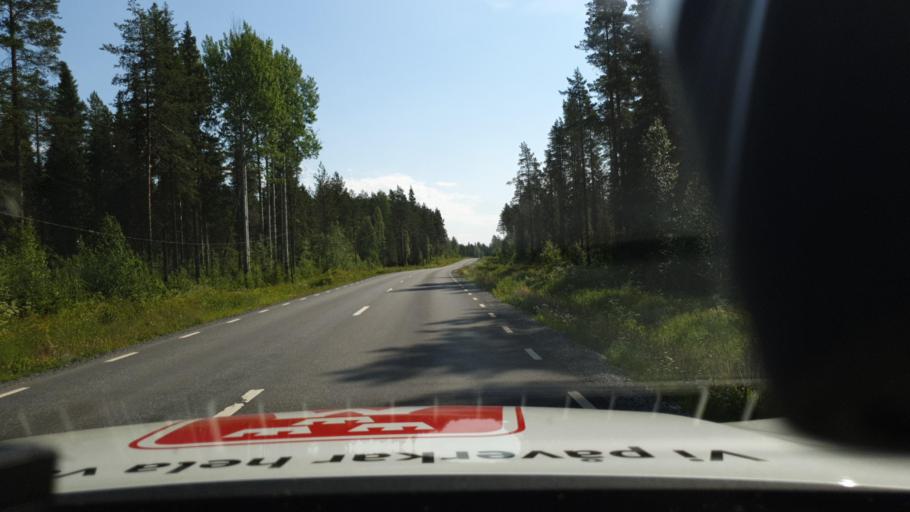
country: SE
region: Norrbotten
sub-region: Lulea Kommun
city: Ranea
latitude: 65.7906
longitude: 22.1296
